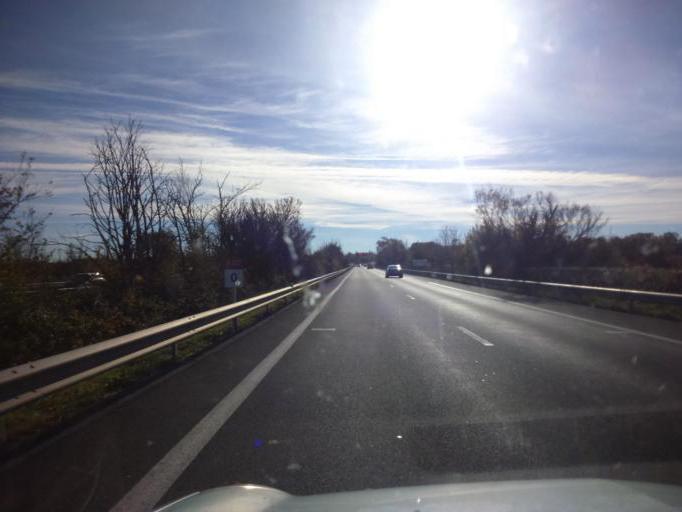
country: FR
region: Poitou-Charentes
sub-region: Departement de la Charente-Maritime
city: Breuil-Magne
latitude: 45.9750
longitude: -0.9915
